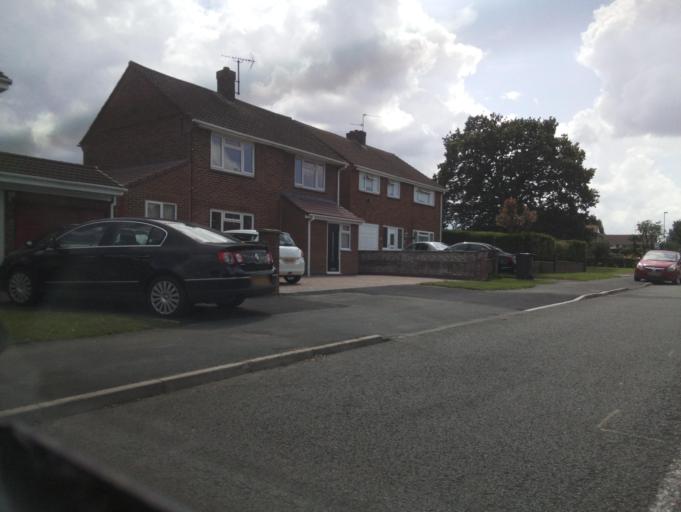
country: GB
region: England
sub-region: Borough of Swindon
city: Swindon
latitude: 51.5458
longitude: -1.7645
